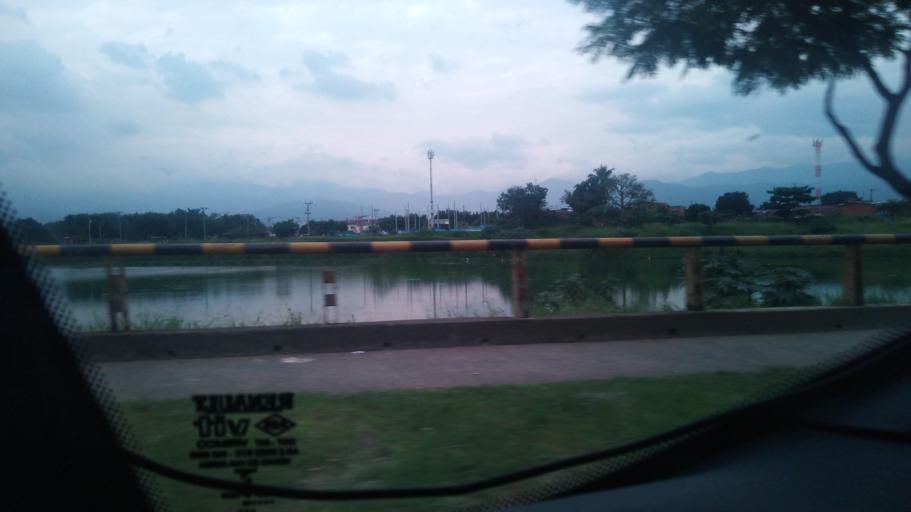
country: CO
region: Valle del Cauca
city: Cali
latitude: 3.4379
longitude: -76.4842
